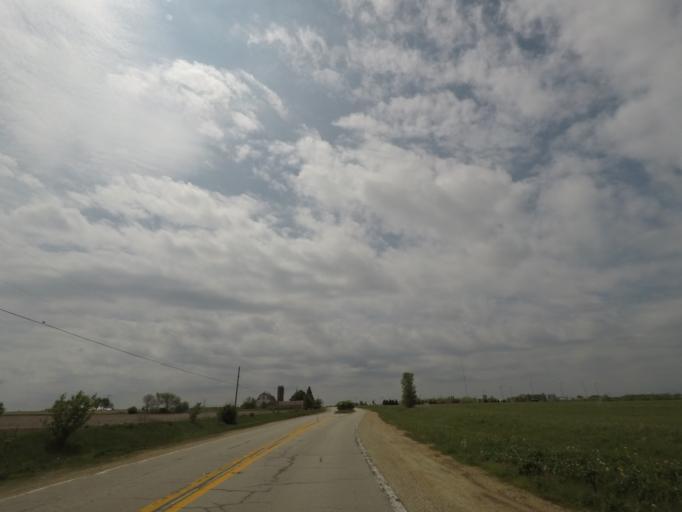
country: US
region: Illinois
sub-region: Winnebago County
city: Machesney Park
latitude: 42.3302
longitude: -88.9501
